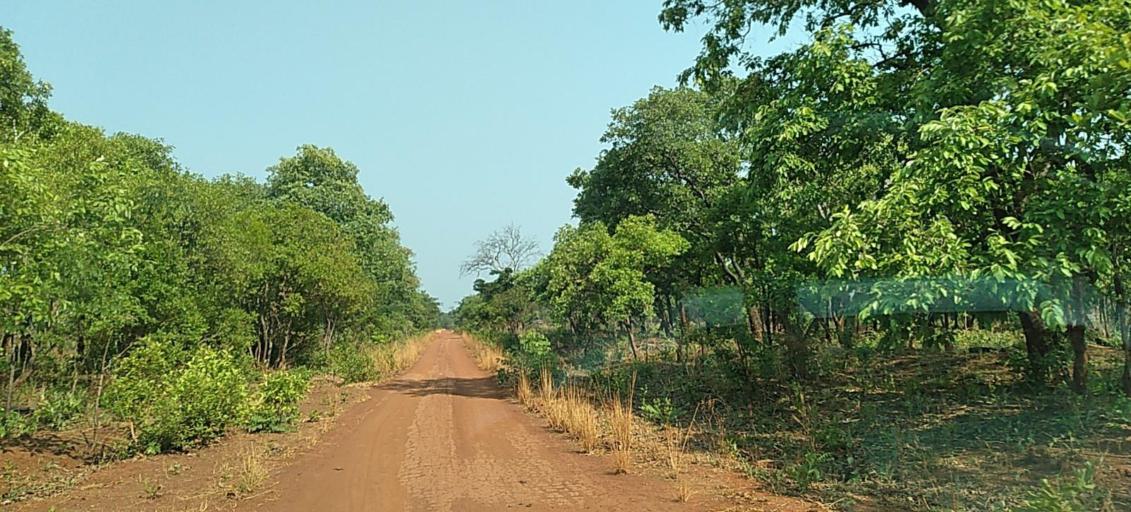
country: ZM
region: Copperbelt
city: Chingola
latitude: -12.8839
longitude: 27.4113
